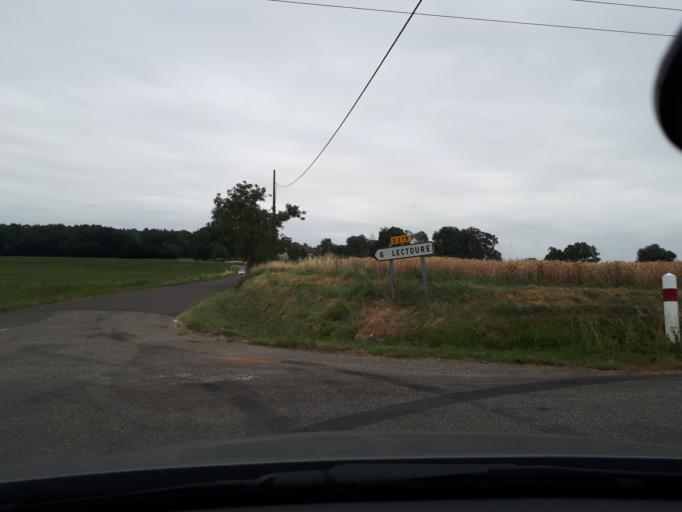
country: FR
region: Midi-Pyrenees
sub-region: Departement du Gers
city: Lectoure
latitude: 43.9625
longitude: 0.6290
